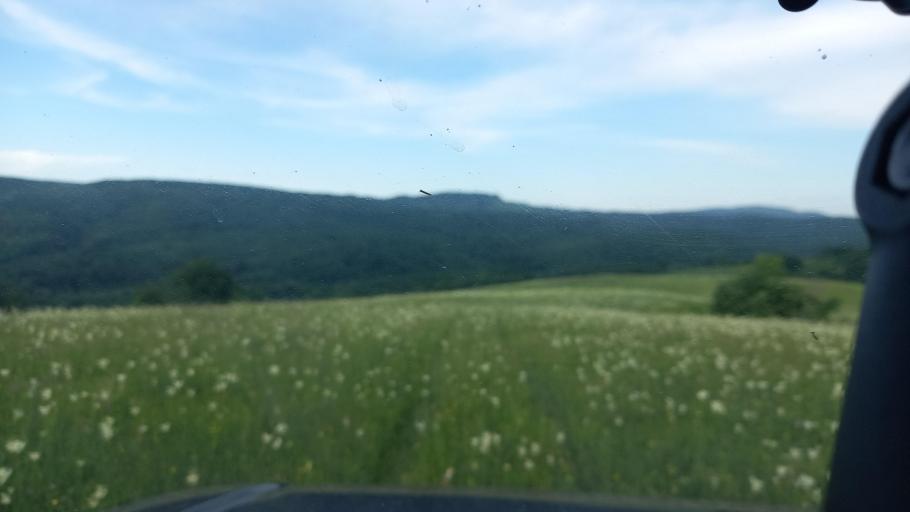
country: RU
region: Karachayevo-Cherkesiya
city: Kurdzhinovo
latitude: 44.1282
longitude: 41.0900
